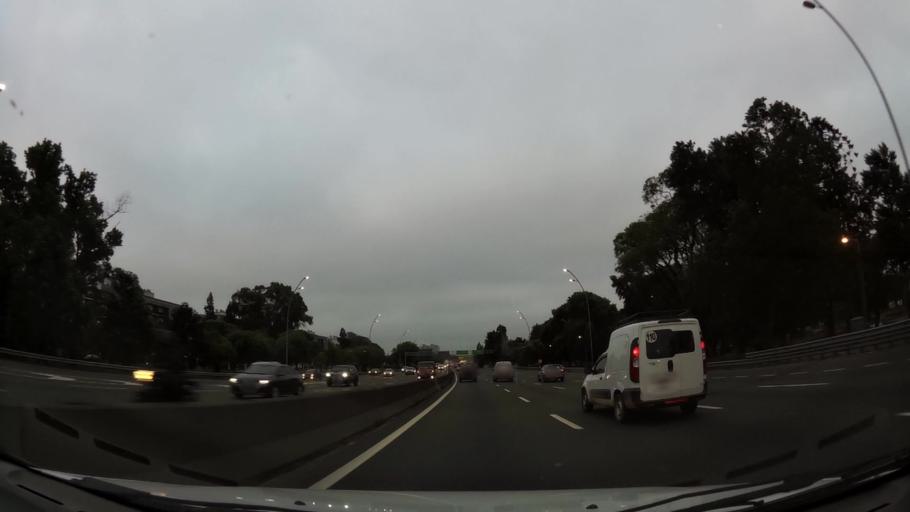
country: AR
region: Buenos Aires
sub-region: Partido de General San Martin
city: General San Martin
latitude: -34.5672
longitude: -58.5080
